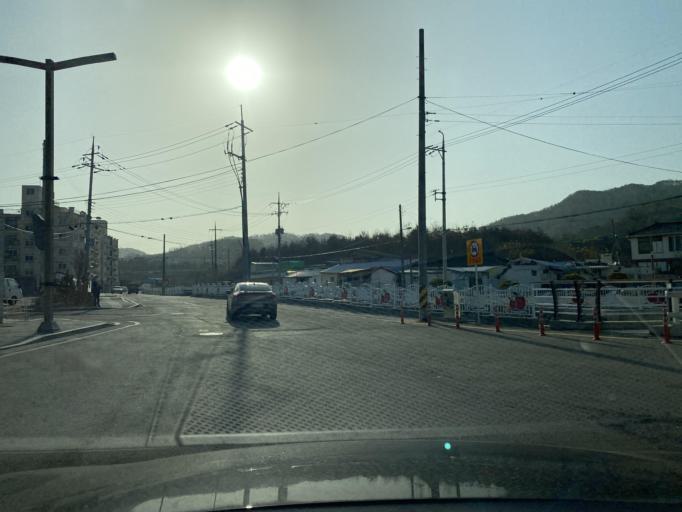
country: KR
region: Chungcheongnam-do
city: Yesan
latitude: 36.6760
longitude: 126.8489
